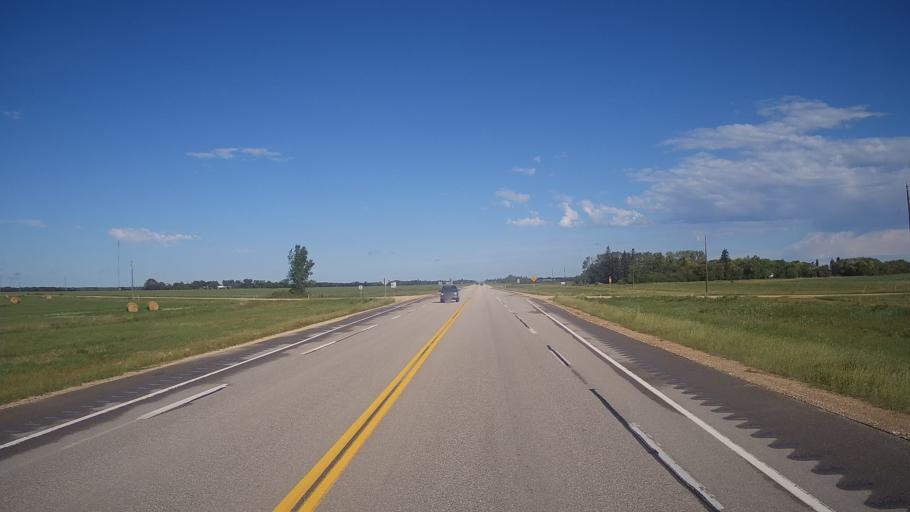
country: CA
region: Manitoba
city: Stonewall
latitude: 50.1811
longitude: -97.6222
